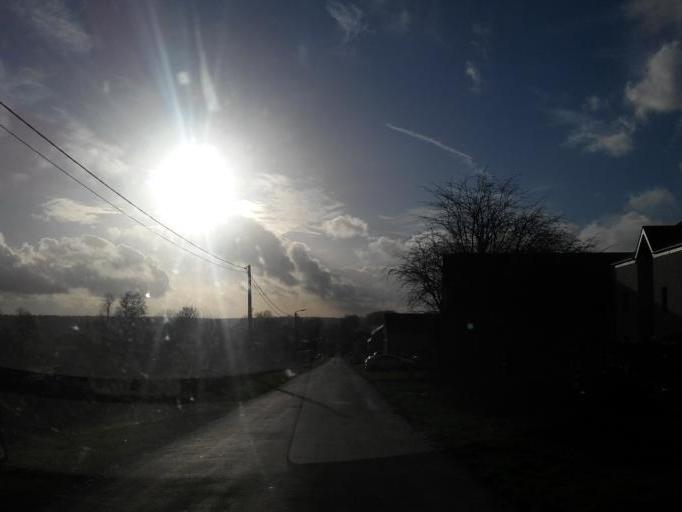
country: BE
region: Wallonia
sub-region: Province du Luxembourg
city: Neufchateau
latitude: 49.8171
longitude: 5.4500
